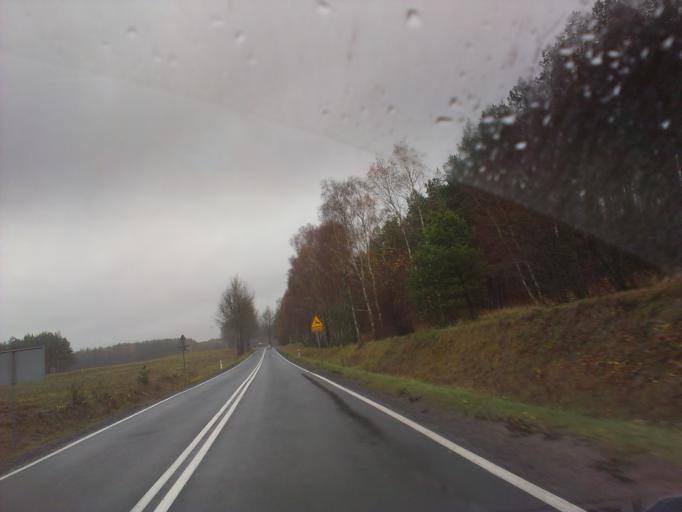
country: PL
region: West Pomeranian Voivodeship
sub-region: Powiat szczecinecki
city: Borne Sulinowo
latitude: 53.6078
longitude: 16.5821
